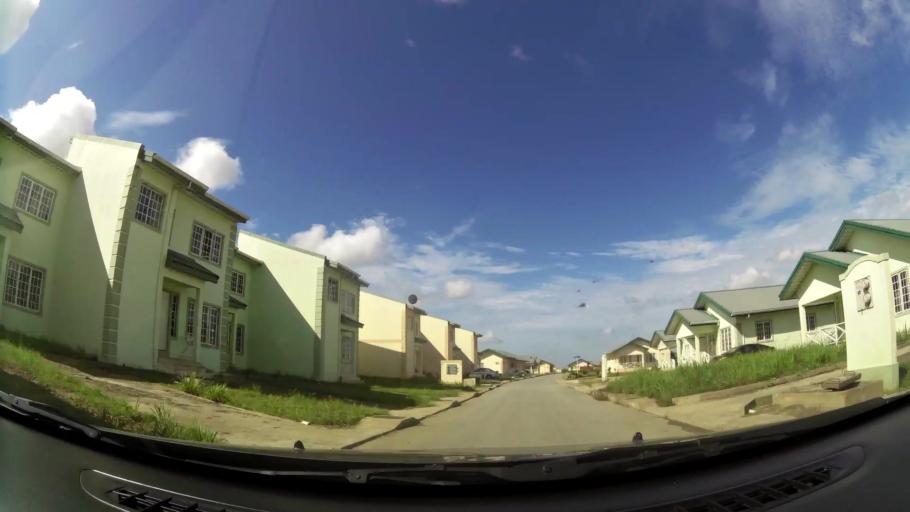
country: TT
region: Chaguanas
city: Chaguanas
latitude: 10.5350
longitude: -61.3929
